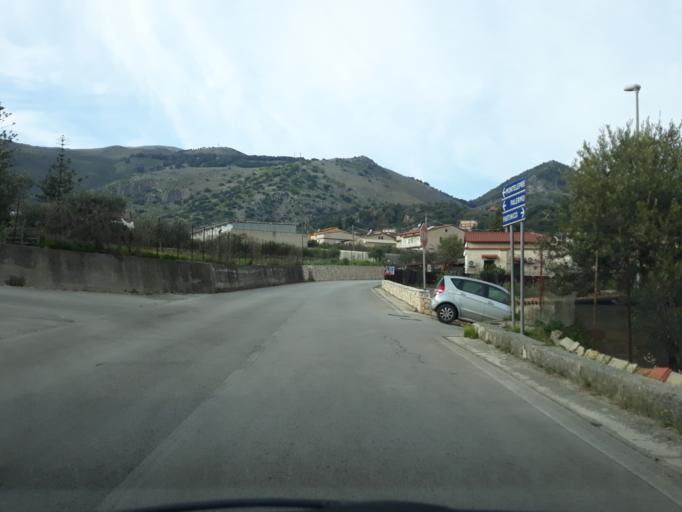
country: IT
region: Sicily
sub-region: Palermo
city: Giardinello
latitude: 38.0831
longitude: 13.1635
